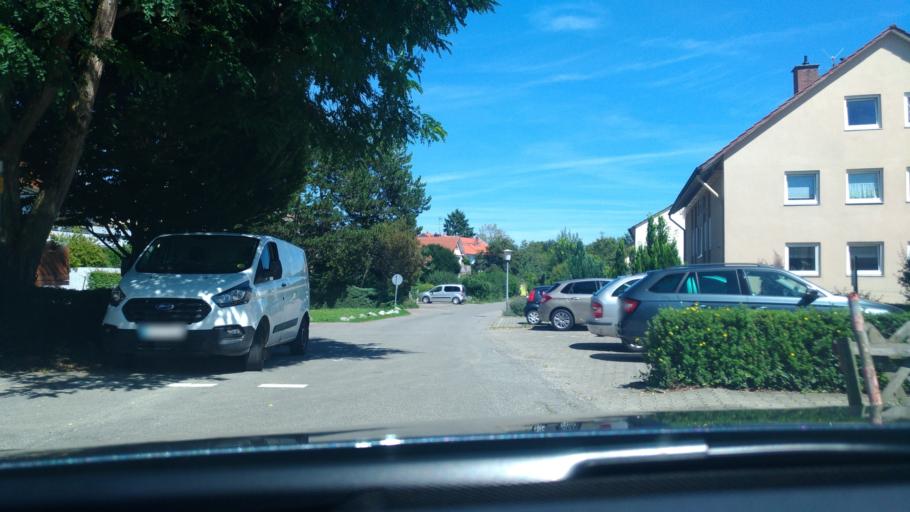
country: DE
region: Baden-Wuerttemberg
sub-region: Tuebingen Region
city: Uberlingen
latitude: 47.7730
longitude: 9.1496
